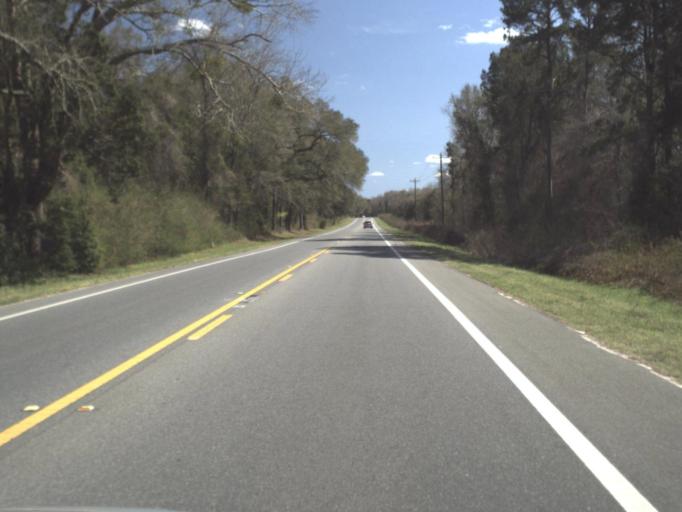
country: US
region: Florida
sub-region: Gadsden County
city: Gretna
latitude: 30.6021
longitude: -84.6527
